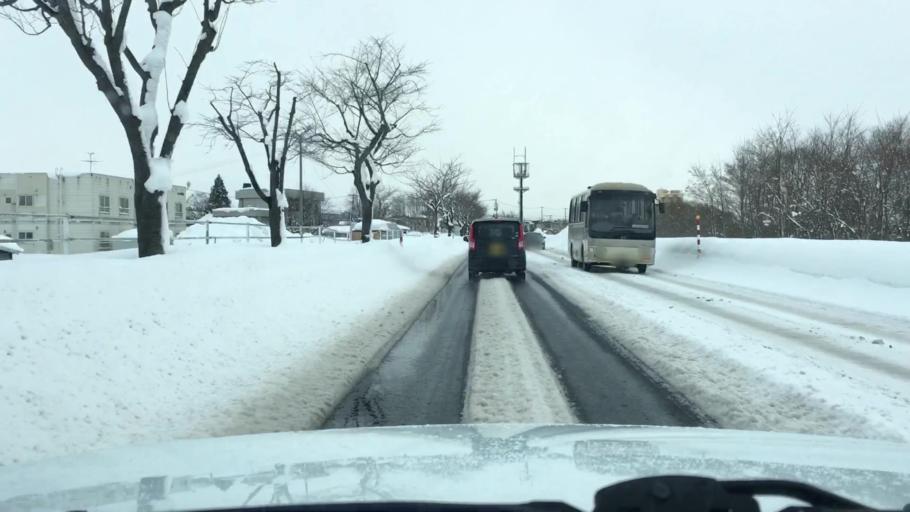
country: JP
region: Aomori
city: Hirosaki
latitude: 40.6127
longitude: 140.4554
